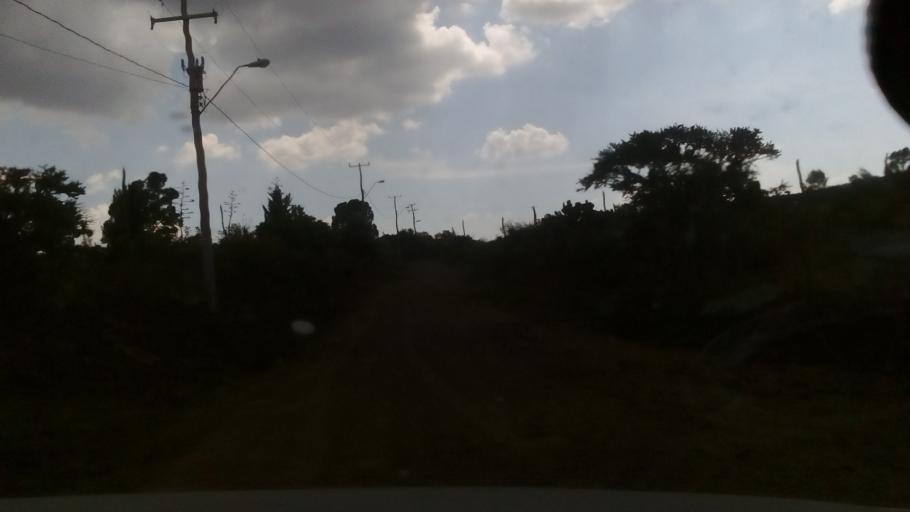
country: MX
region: Guanajuato
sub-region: Silao de la Victoria
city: San Francisco (Banos de Agua Caliente)
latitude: 21.1713
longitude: -101.4152
